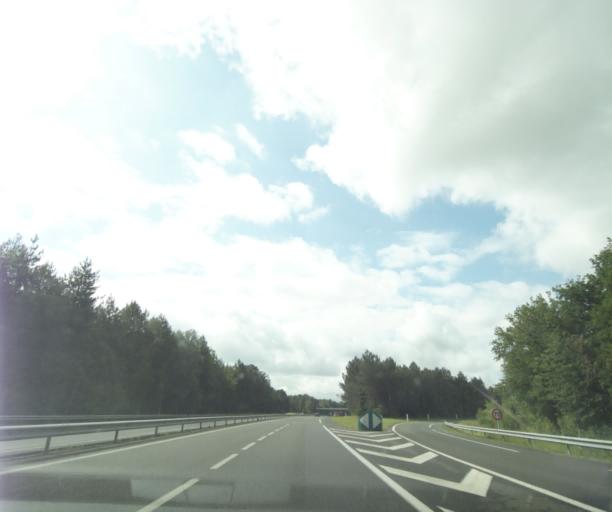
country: FR
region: Pays de la Loire
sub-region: Departement de Maine-et-Loire
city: Seiches-sur-le-Loir
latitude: 47.5676
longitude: -0.3322
